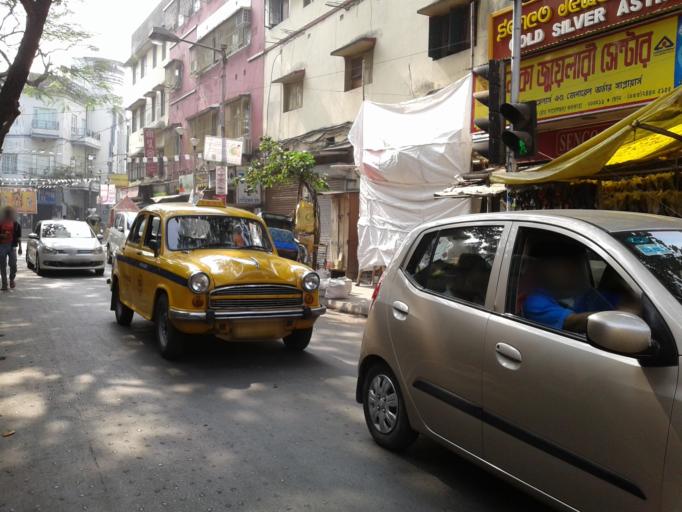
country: IN
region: West Bengal
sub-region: Kolkata
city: Kolkata
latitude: 22.5204
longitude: 88.3679
